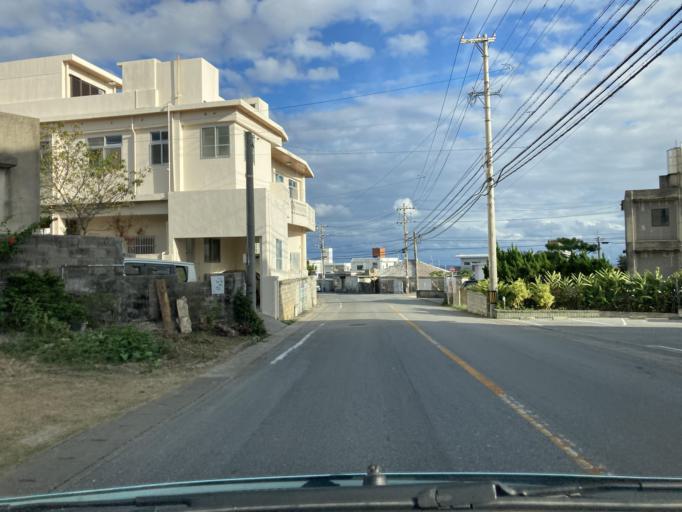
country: JP
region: Okinawa
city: Itoman
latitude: 26.1270
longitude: 127.7574
